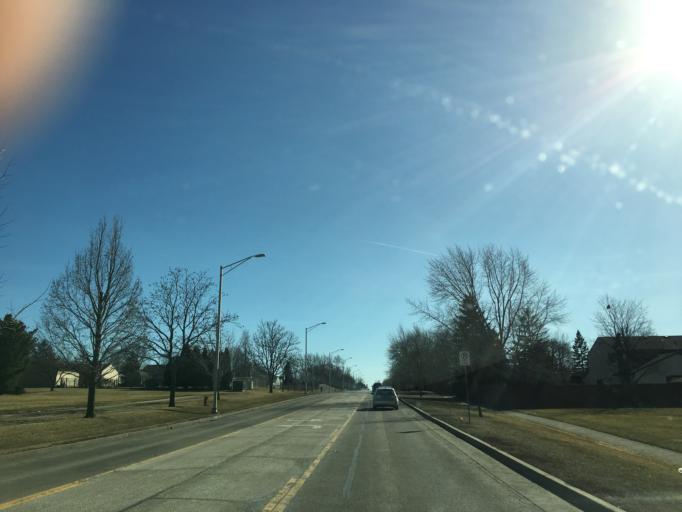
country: US
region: Illinois
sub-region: Cook County
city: Schaumburg
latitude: 42.0311
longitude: -88.1192
